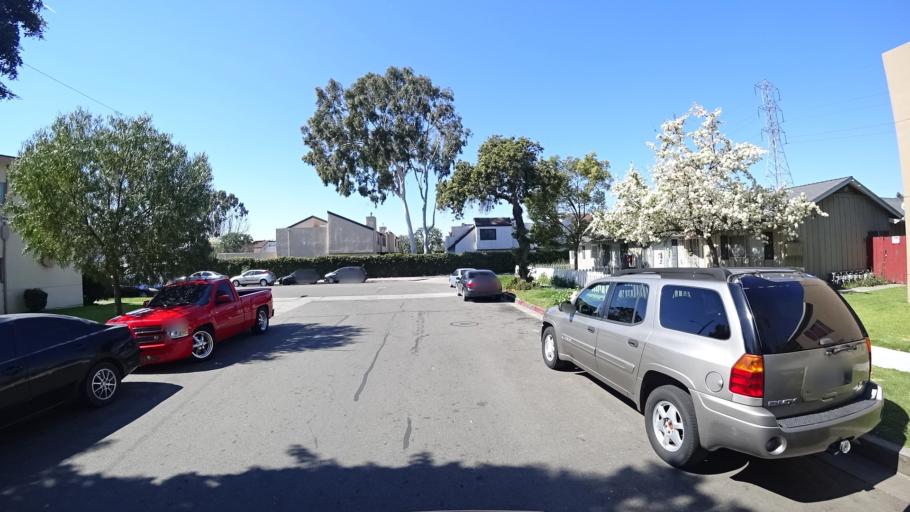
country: US
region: California
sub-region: Orange County
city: Garden Grove
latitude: 33.8063
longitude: -117.9476
